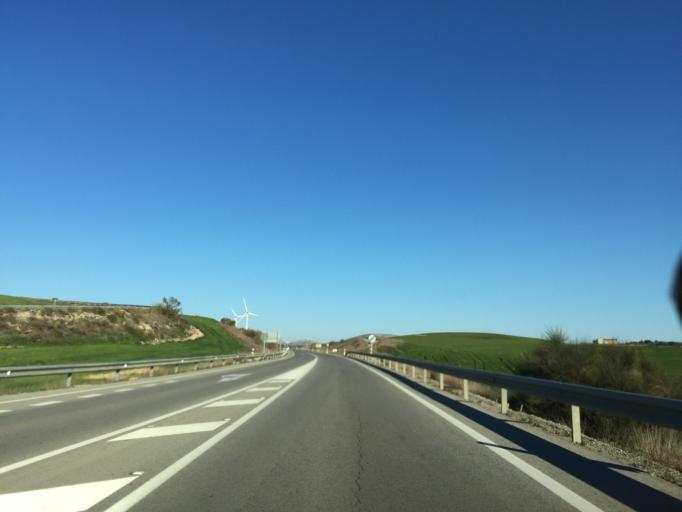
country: ES
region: Andalusia
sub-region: Provincia de Malaga
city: Ardales
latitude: 36.9226
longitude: -4.8457
